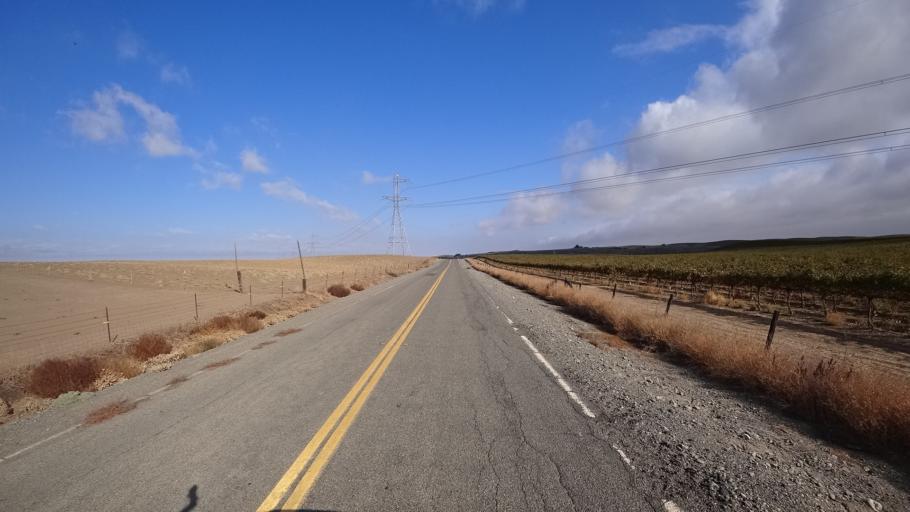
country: US
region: California
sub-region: Yolo County
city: Esparto
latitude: 38.7882
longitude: -122.0073
